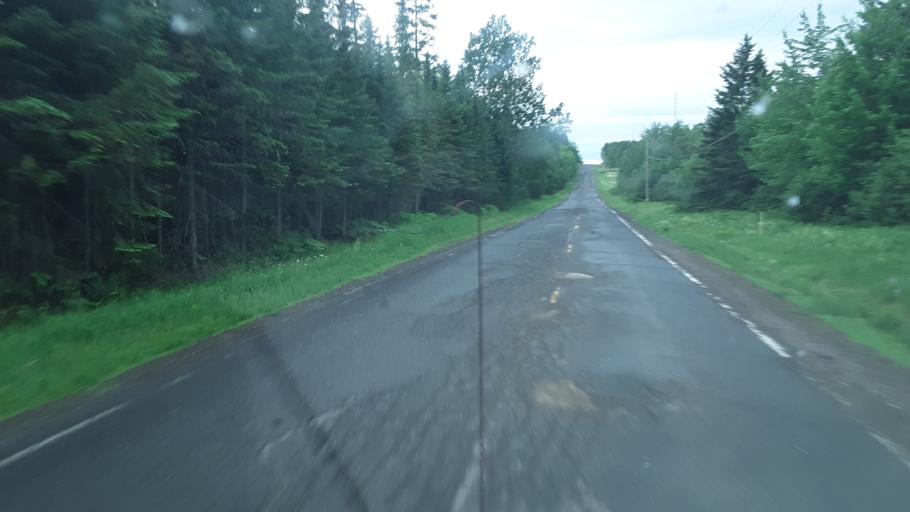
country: US
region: Maine
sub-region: Aroostook County
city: Caribou
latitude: 46.8788
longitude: -68.2035
